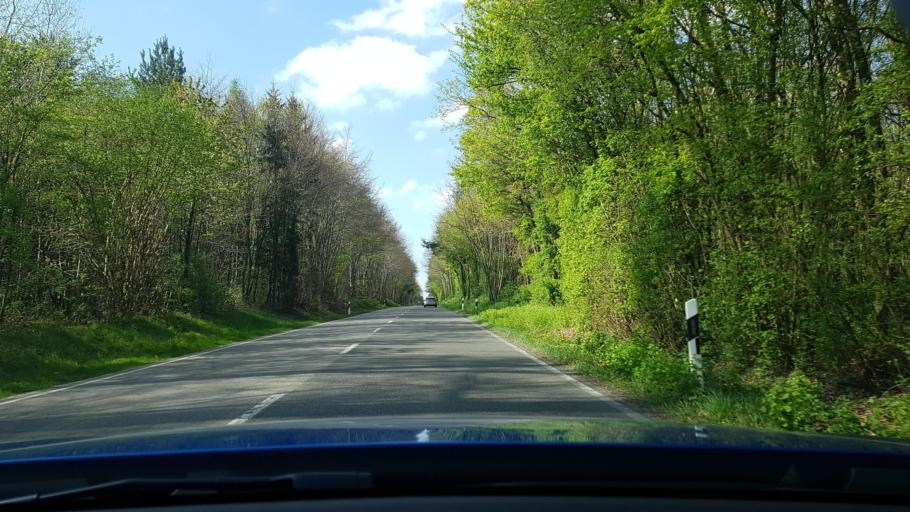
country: LU
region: Luxembourg
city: Bereldange
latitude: 49.6353
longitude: 6.1085
